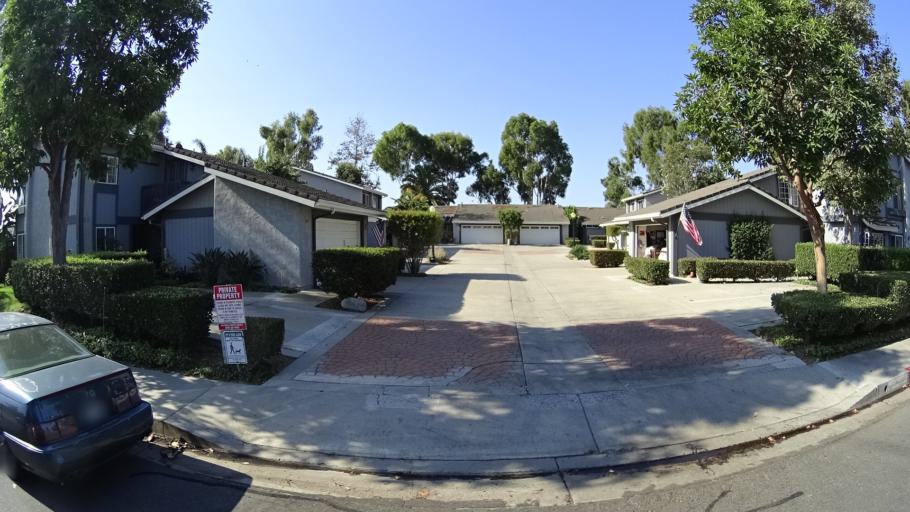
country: US
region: California
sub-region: Orange County
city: San Clemente
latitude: 33.4510
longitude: -117.6527
